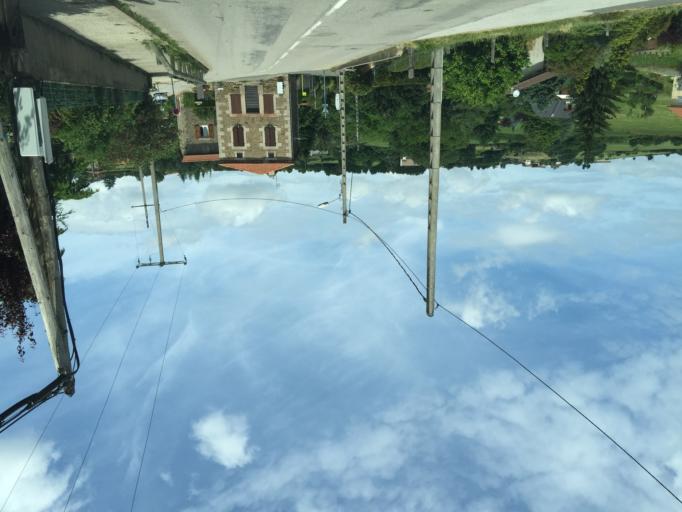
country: FR
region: Rhone-Alpes
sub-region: Departement de la Loire
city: Sorbiers
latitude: 45.4905
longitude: 4.4860
